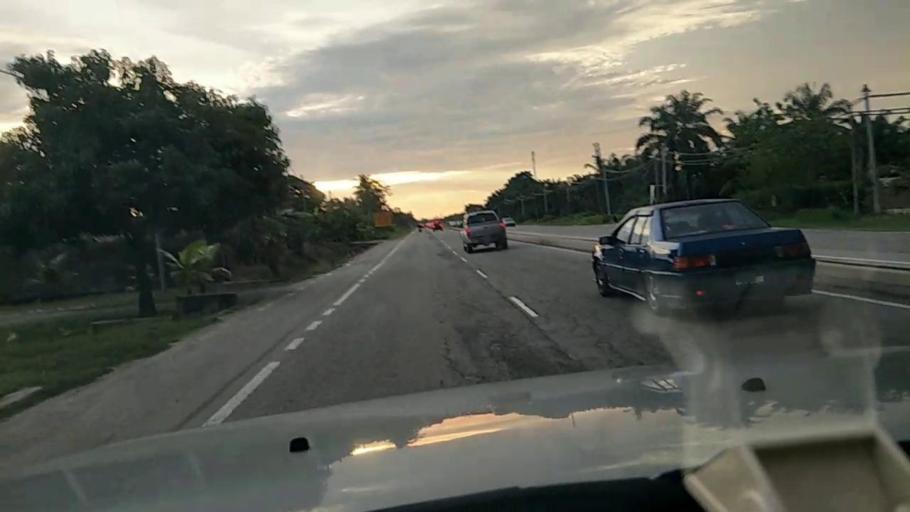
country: MY
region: Perak
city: Kampong Dungun
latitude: 3.1446
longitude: 101.3539
